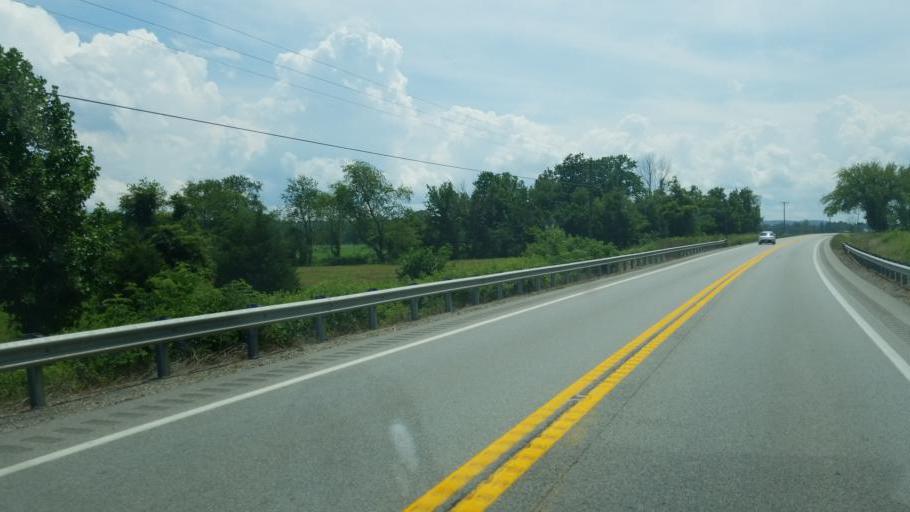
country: US
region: West Virginia
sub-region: Putnam County
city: Buffalo
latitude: 38.6526
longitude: -81.9702
